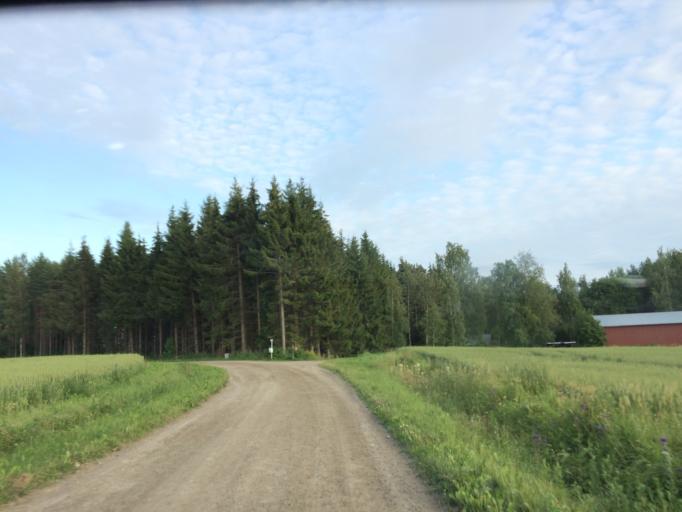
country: FI
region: Haeme
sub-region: Haemeenlinna
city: Janakkala
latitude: 60.8777
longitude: 24.6175
